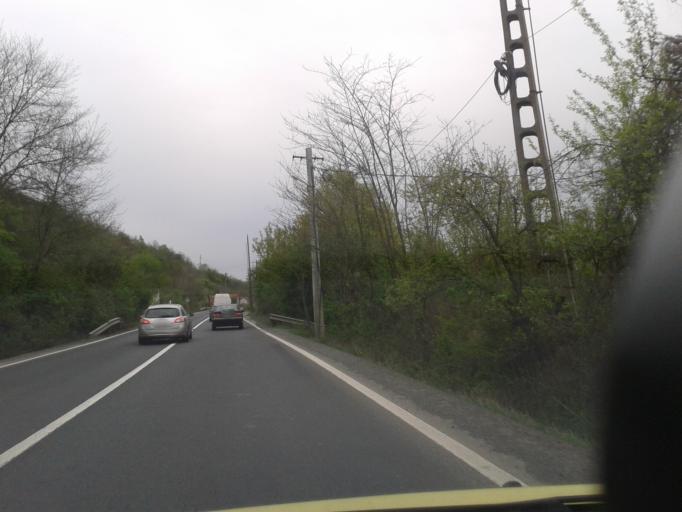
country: RO
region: Arad
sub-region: Comuna Bata
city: Bata
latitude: 46.0545
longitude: 22.0480
